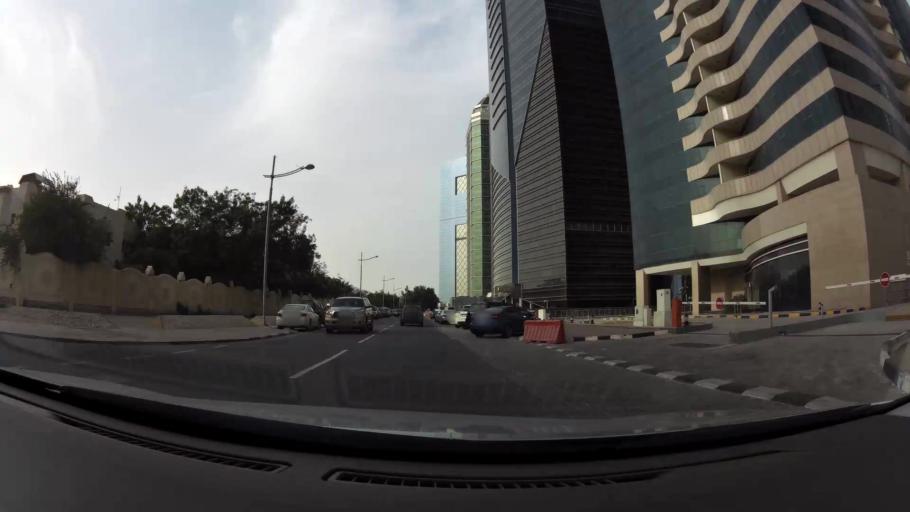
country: QA
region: Baladiyat ad Dawhah
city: Doha
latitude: 25.3256
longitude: 51.5241
